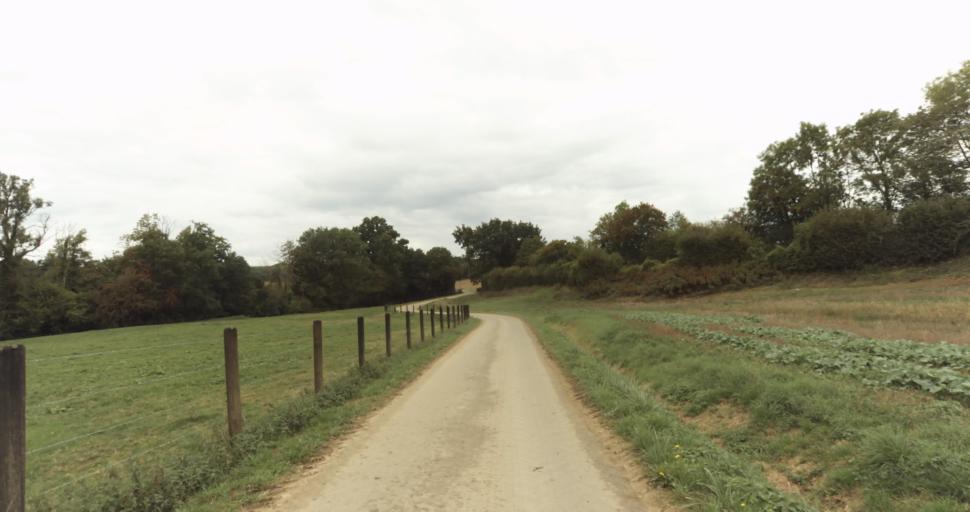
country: FR
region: Lower Normandy
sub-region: Departement de l'Orne
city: Gace
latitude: 48.6871
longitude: 0.2760
